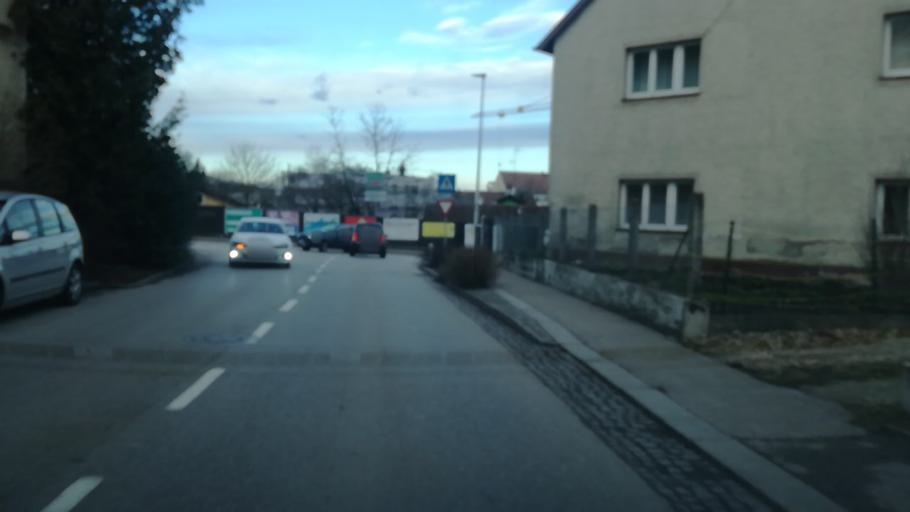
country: AT
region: Upper Austria
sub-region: Politischer Bezirk Ried im Innkreis
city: Ried im Innkreis
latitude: 48.2054
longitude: 13.4851
